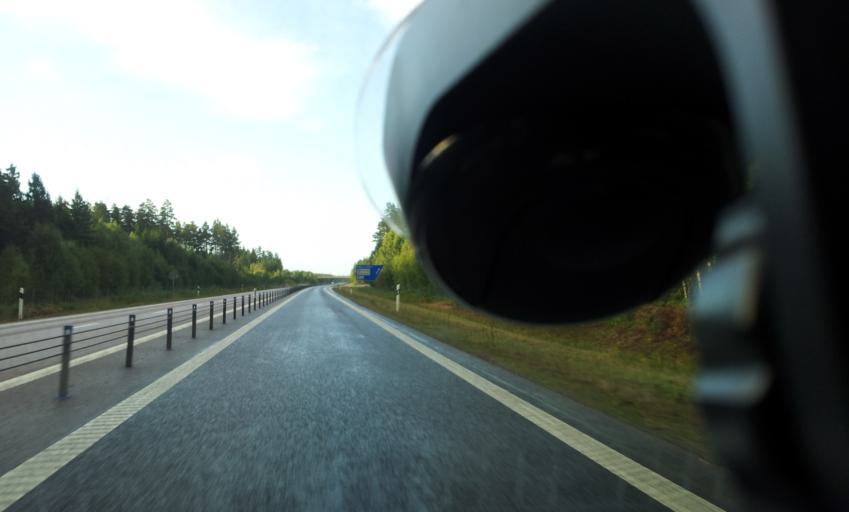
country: SE
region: Kalmar
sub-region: Torsas Kommun
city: Torsas
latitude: 56.5092
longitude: 16.0863
